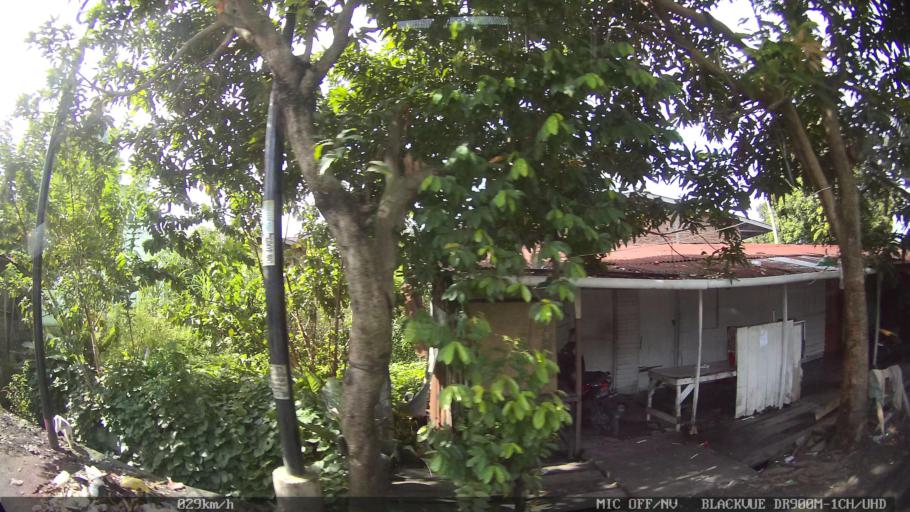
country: ID
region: North Sumatra
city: Medan
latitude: 3.6117
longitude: 98.6499
